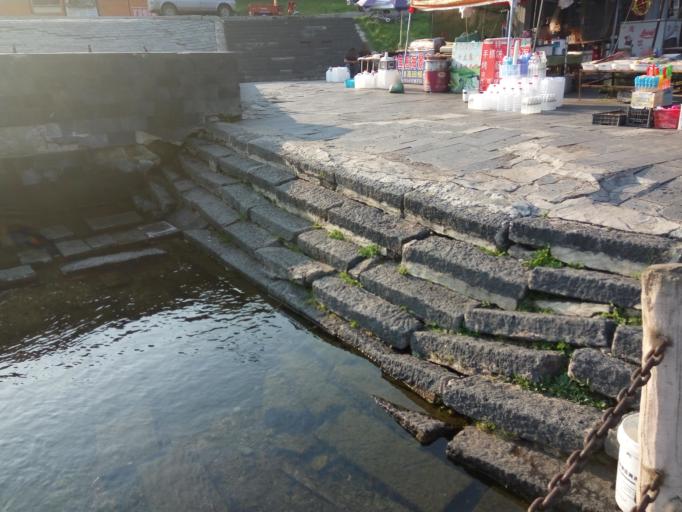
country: CN
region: Heilongjiang Sheng
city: Erjing
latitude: 48.6496
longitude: 126.1312
